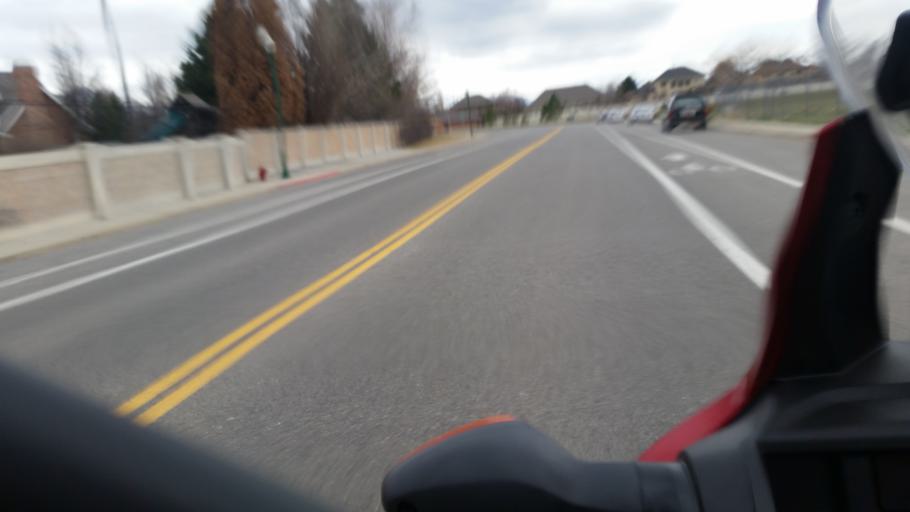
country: US
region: Utah
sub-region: Utah County
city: Orem
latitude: 40.3223
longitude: -111.6881
